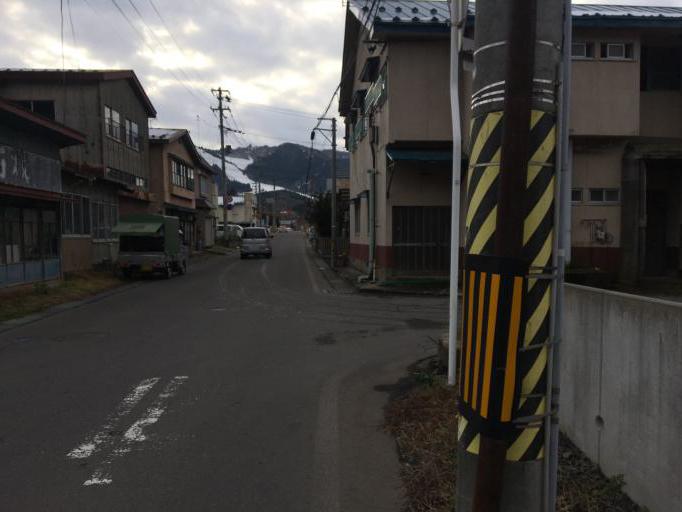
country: JP
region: Aomori
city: Hirosaki
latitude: 40.5224
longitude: 140.5635
